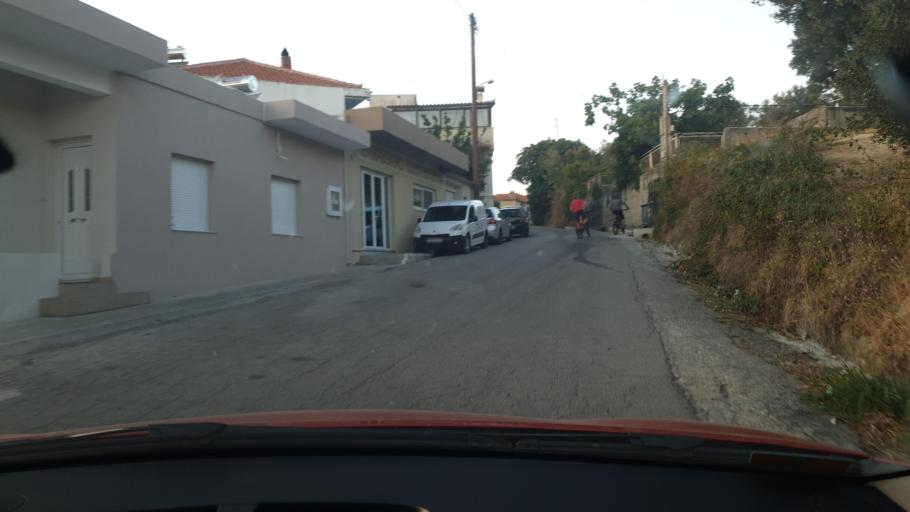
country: GR
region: Central Greece
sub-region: Nomos Evvoias
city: Oxilithos
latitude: 38.5821
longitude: 24.1108
